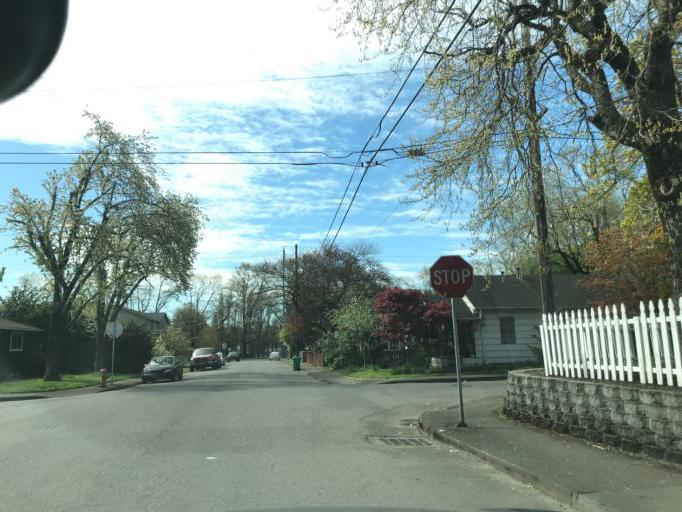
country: US
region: Oregon
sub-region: Multnomah County
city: Lents
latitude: 45.4912
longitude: -122.5696
